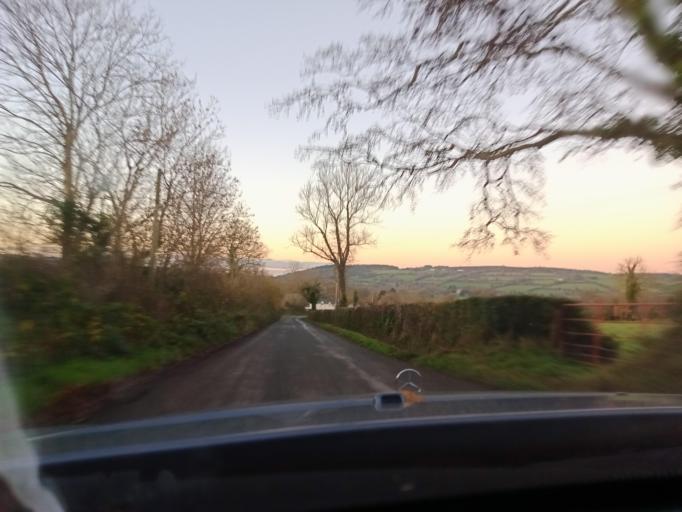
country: IE
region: Leinster
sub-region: Kilkenny
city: Thomastown
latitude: 52.4858
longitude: -7.1016
